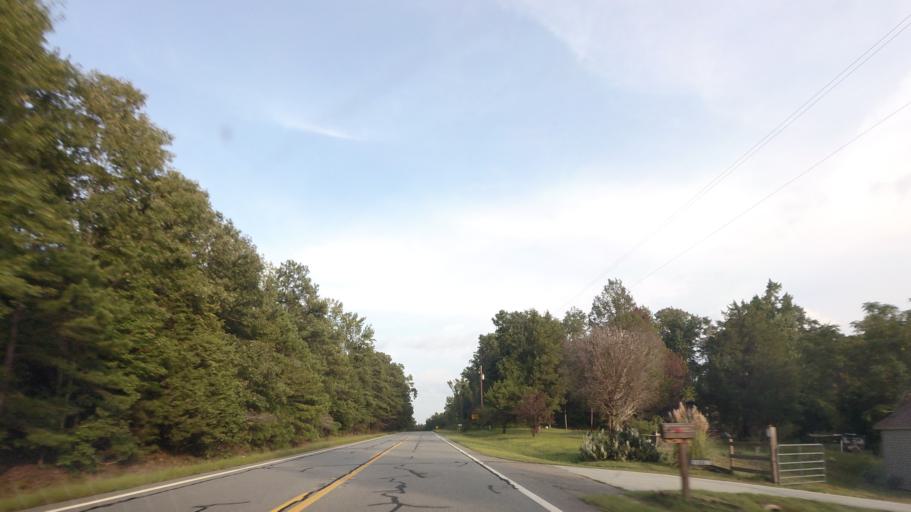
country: US
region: Georgia
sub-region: Wilkinson County
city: Gordon
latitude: 32.8611
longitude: -83.3639
